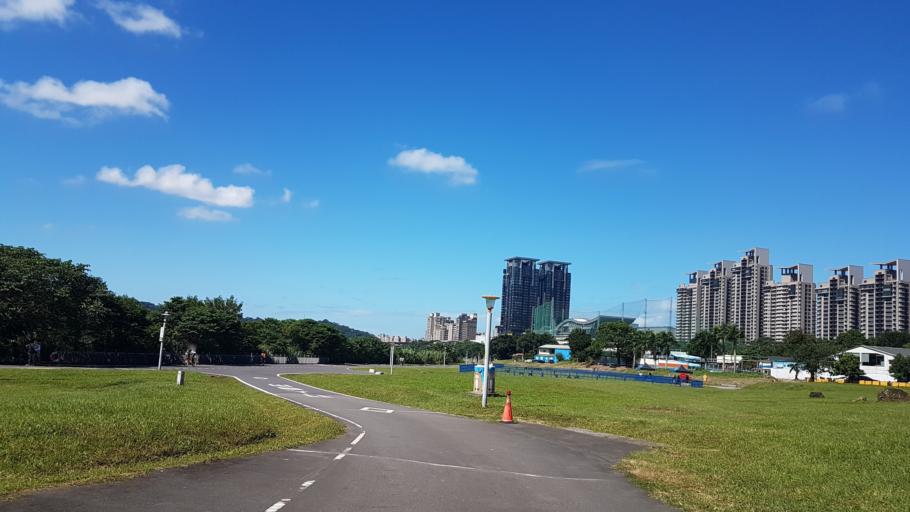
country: TW
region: Taipei
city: Taipei
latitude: 24.9651
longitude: 121.5353
